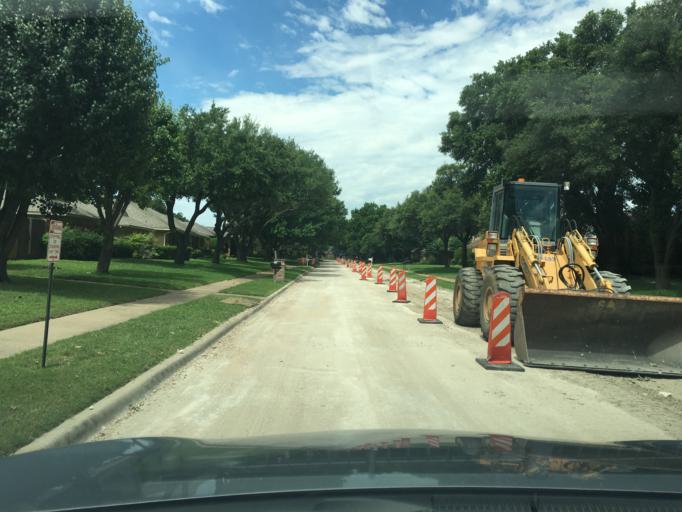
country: US
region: Texas
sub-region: Dallas County
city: Richardson
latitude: 32.9344
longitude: -96.6960
